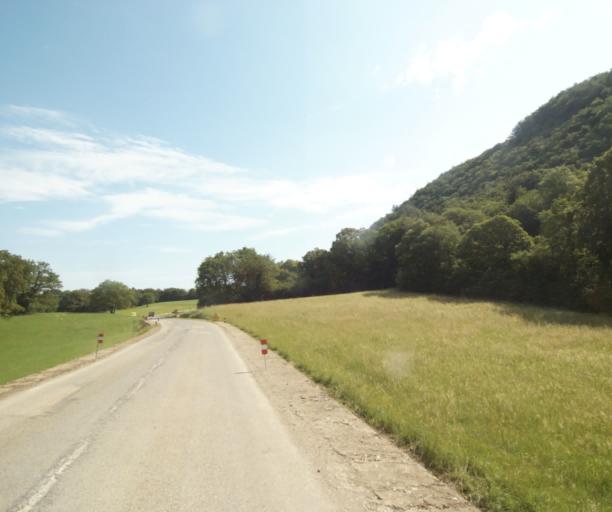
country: FR
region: Rhone-Alpes
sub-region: Departement de la Haute-Savoie
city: Lyaud
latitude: 46.3309
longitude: 6.5100
